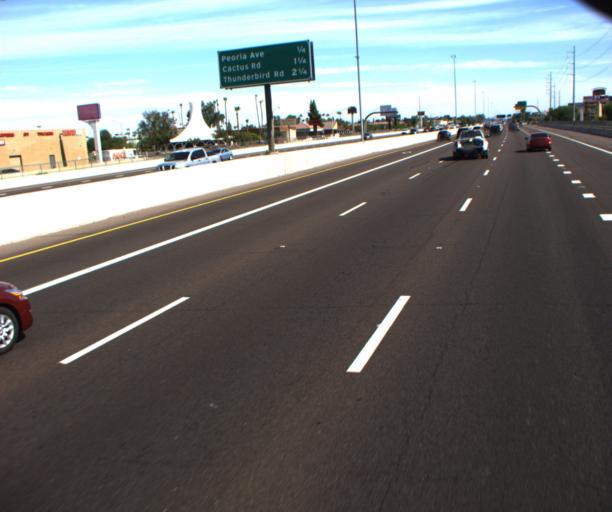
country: US
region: Arizona
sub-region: Maricopa County
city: Glendale
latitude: 33.5746
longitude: -112.1169
